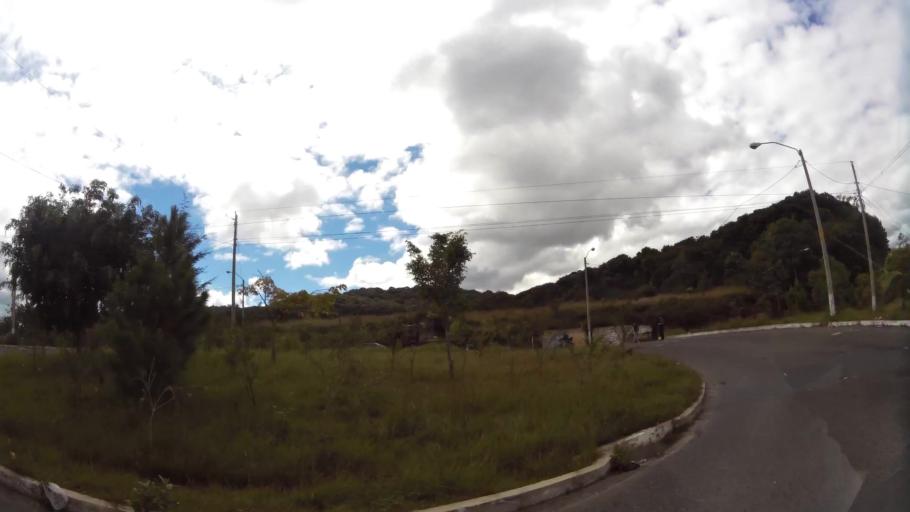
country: GT
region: Guatemala
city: Guatemala City
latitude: 14.6616
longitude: -90.5525
